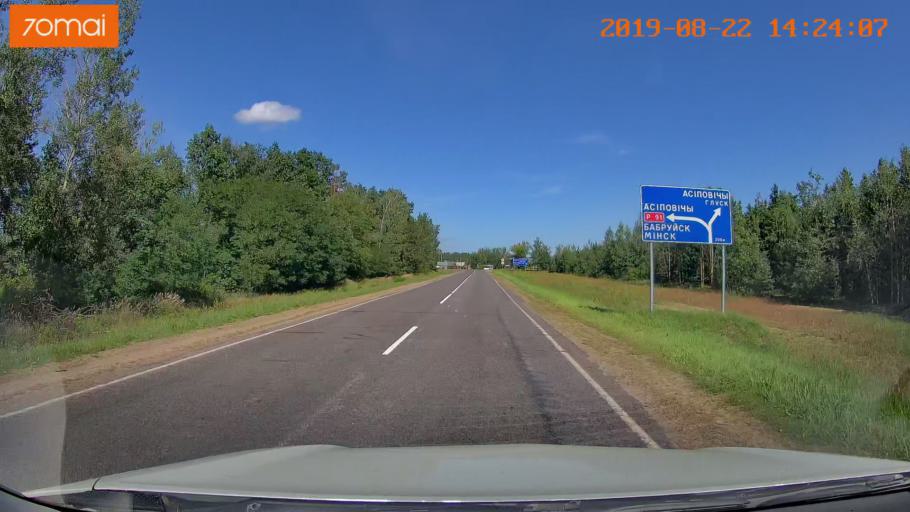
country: BY
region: Mogilev
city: Asipovichy
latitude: 53.2963
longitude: 28.5945
